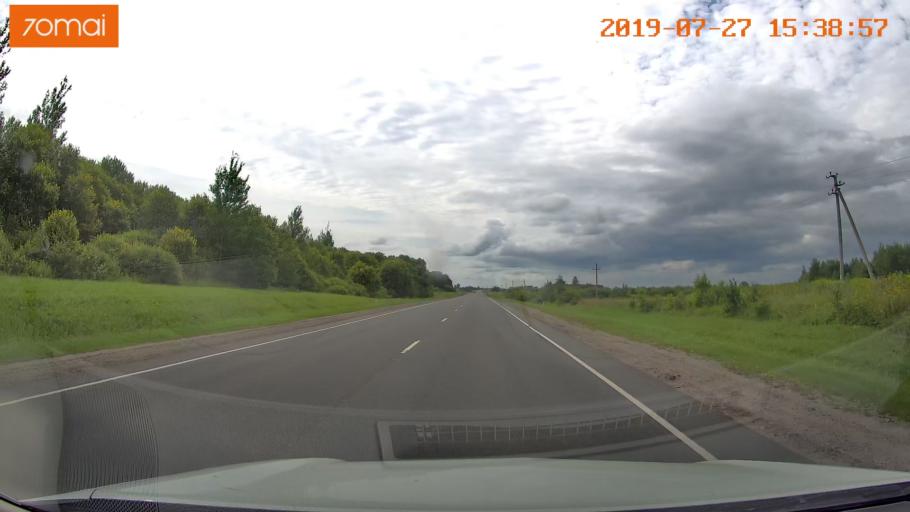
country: RU
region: Kaliningrad
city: Gusev
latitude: 54.6067
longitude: 22.3006
